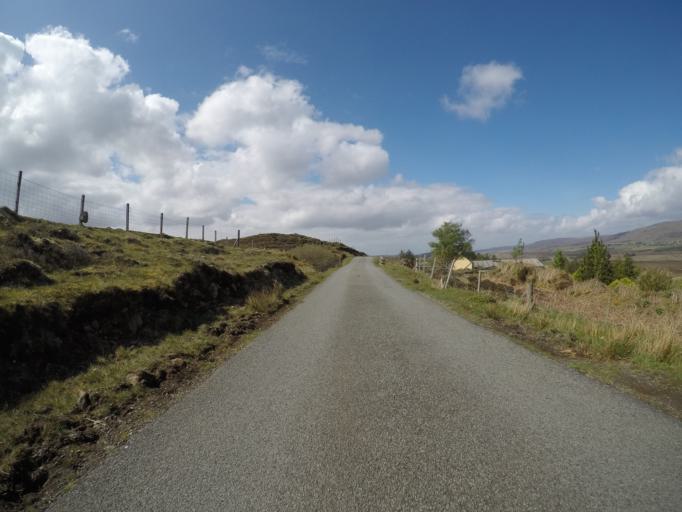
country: GB
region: Scotland
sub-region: Highland
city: Isle of Skye
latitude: 57.4240
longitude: -6.2674
